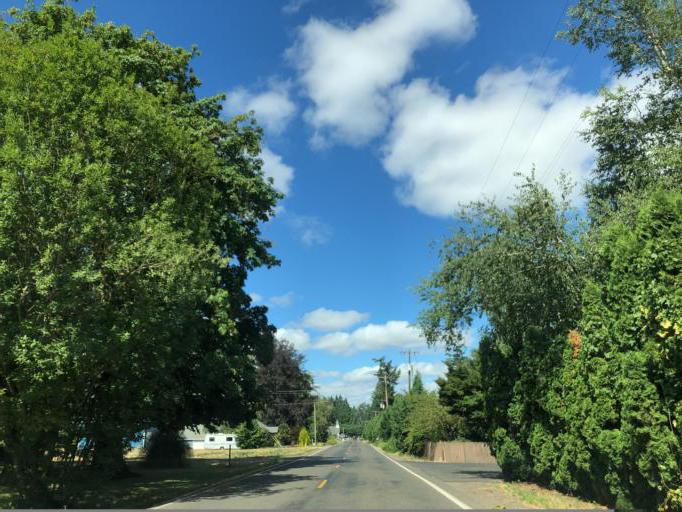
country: US
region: Oregon
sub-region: Marion County
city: Mount Angel
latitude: 45.1003
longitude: -122.7382
